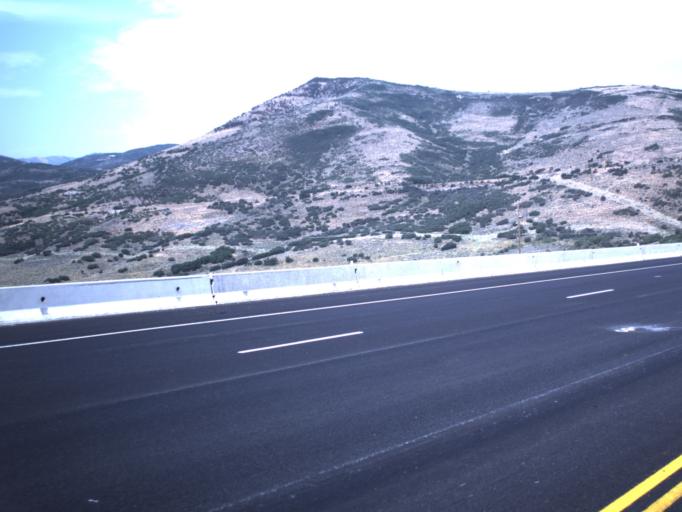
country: US
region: Utah
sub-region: Summit County
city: Park City
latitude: 40.6557
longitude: -111.4117
